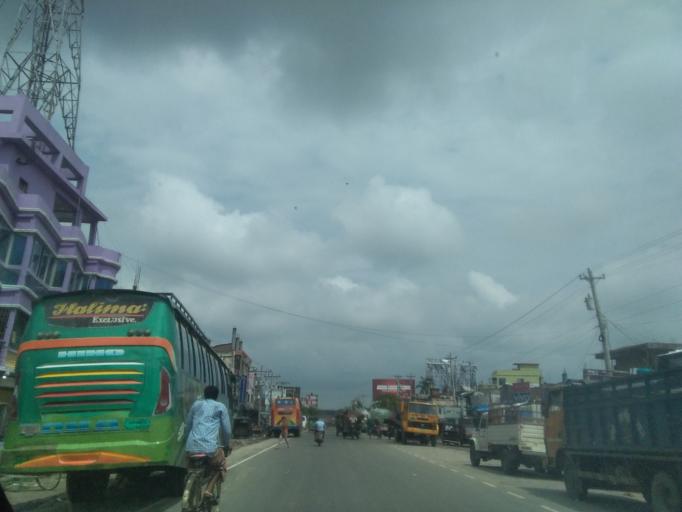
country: BD
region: Khulna
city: Kesabpur
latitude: 22.8401
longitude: 89.2968
